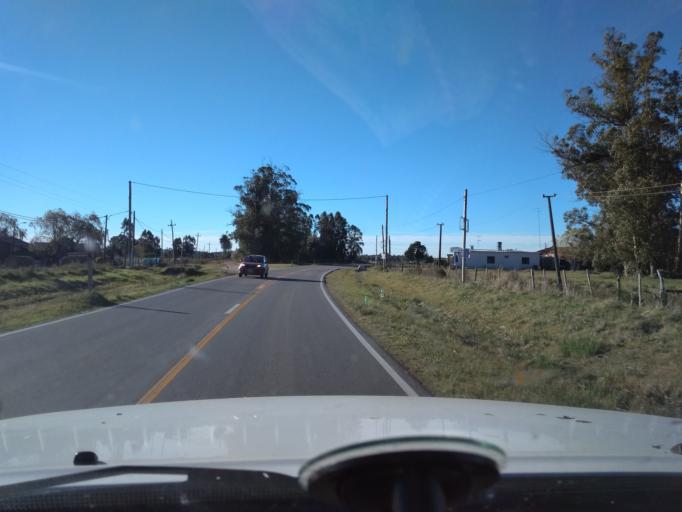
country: UY
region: Canelones
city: Santa Rosa
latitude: -34.5114
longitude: -56.0540
